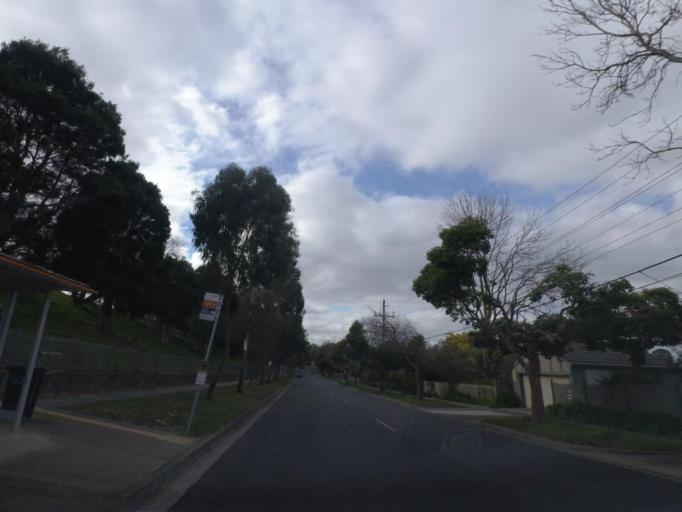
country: AU
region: Victoria
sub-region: Maroondah
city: Ringwood East
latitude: -37.8011
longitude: 145.2391
